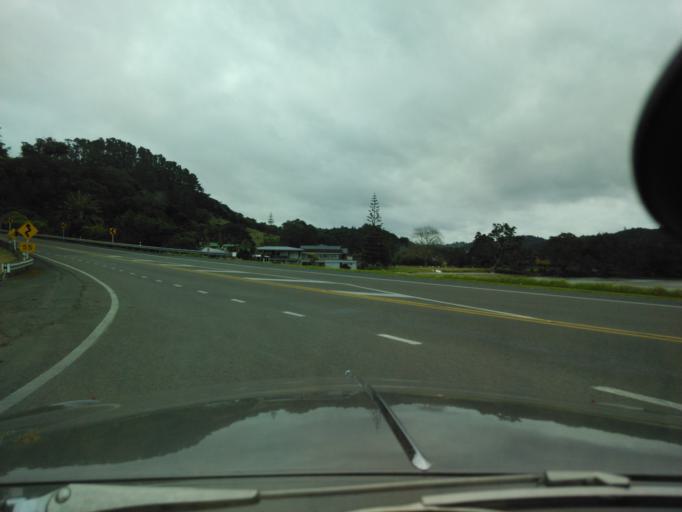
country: NZ
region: Auckland
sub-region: Auckland
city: Warkworth
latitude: -36.5423
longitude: 174.7044
